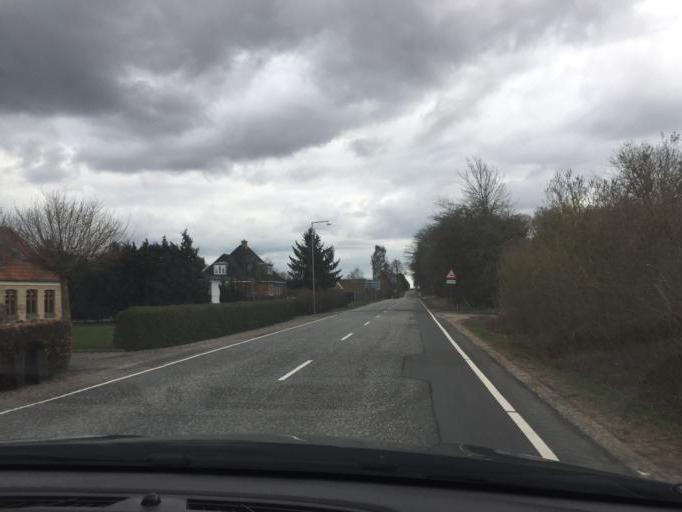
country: DK
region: South Denmark
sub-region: Kerteminde Kommune
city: Langeskov
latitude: 55.3052
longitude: 10.5900
